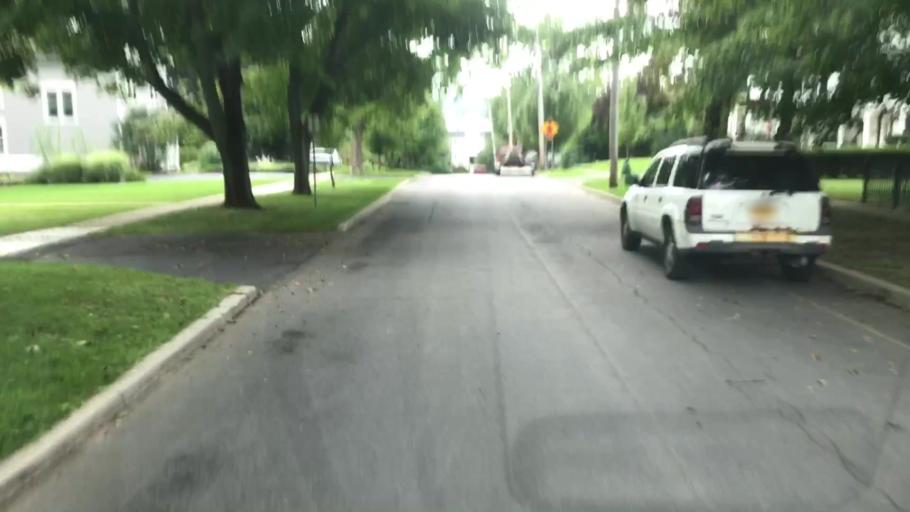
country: US
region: New York
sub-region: Onondaga County
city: Skaneateles
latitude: 42.9472
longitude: -76.4235
